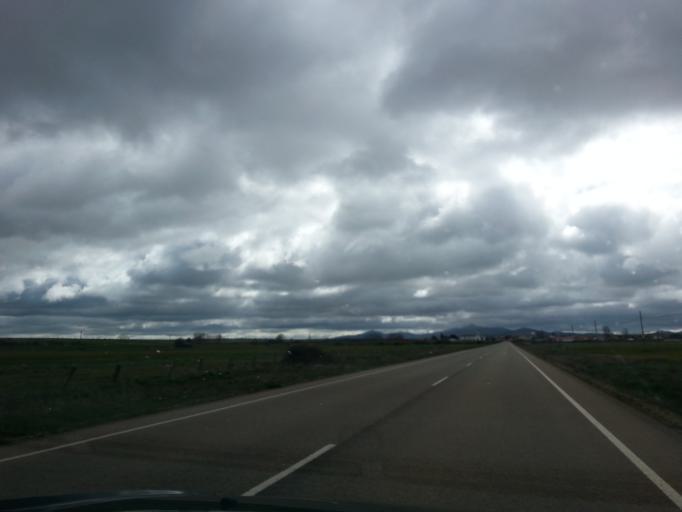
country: ES
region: Castille and Leon
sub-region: Provincia de Salamanca
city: Abusejo
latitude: 40.7185
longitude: -6.1482
